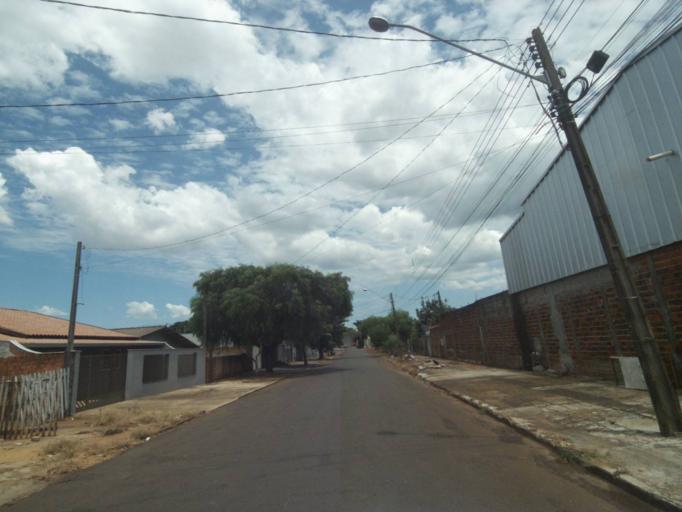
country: BR
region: Parana
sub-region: Londrina
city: Londrina
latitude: -23.3069
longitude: -51.2206
